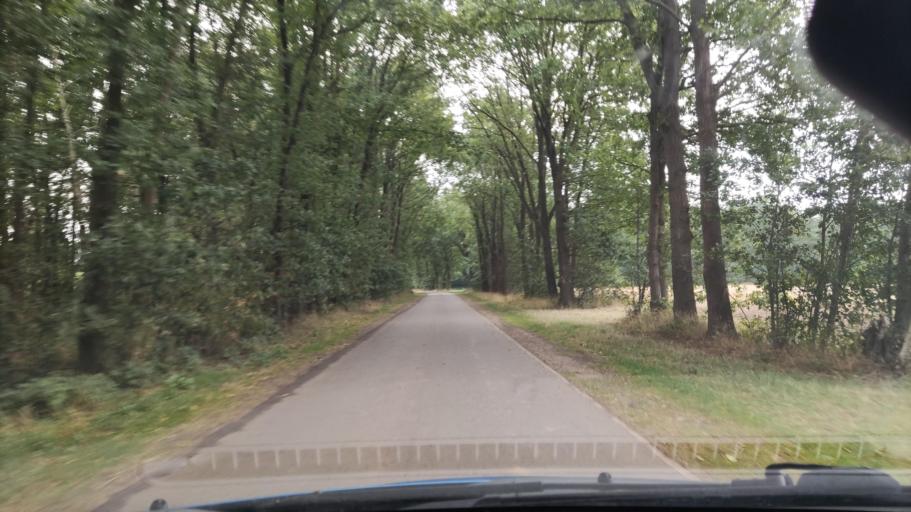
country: DE
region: Lower Saxony
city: Wittorf
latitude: 53.3463
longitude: 10.3732
